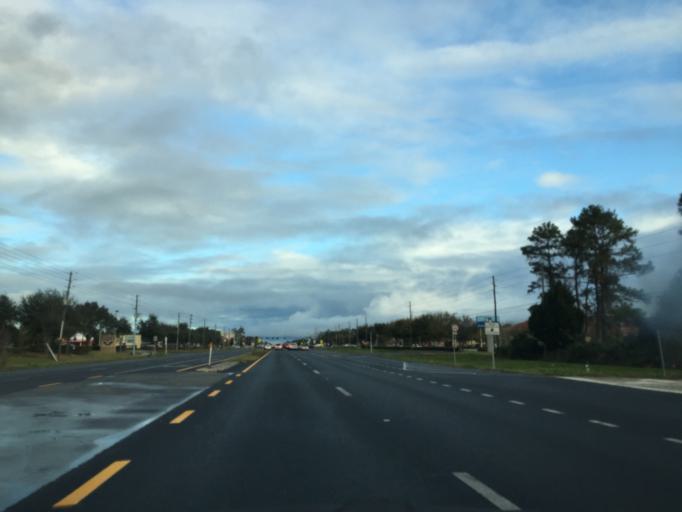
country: US
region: Florida
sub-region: Orange County
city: Bithlo
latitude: 28.5619
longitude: -81.1335
